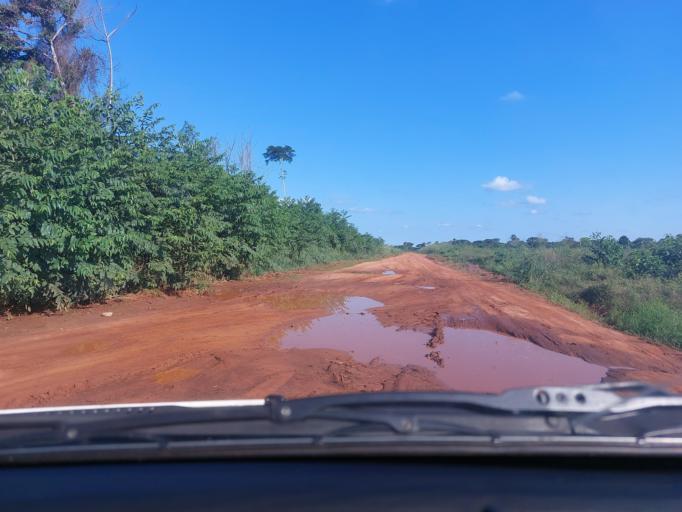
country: PY
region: San Pedro
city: Guayaybi
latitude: -24.5234
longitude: -56.5454
